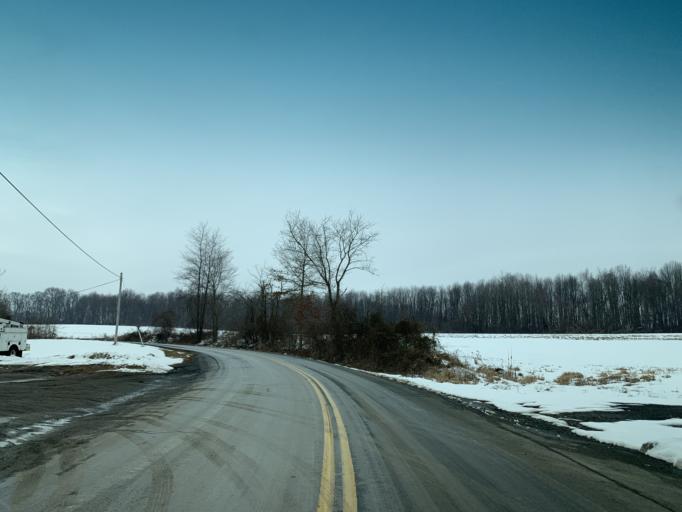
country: US
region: Pennsylvania
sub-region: York County
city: Susquehanna Trails
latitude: 39.7188
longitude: -76.3455
